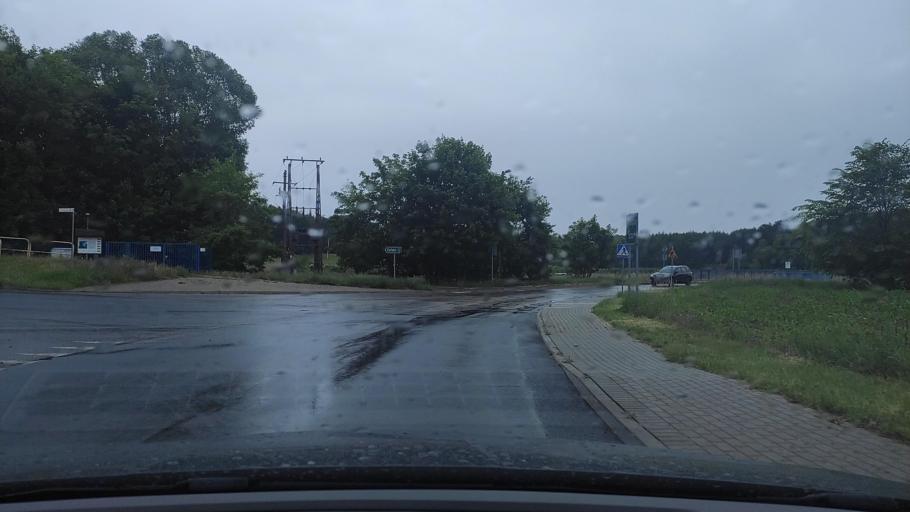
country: PL
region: Greater Poland Voivodeship
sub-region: Powiat poznanski
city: Kostrzyn
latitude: 52.4771
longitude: 17.1847
